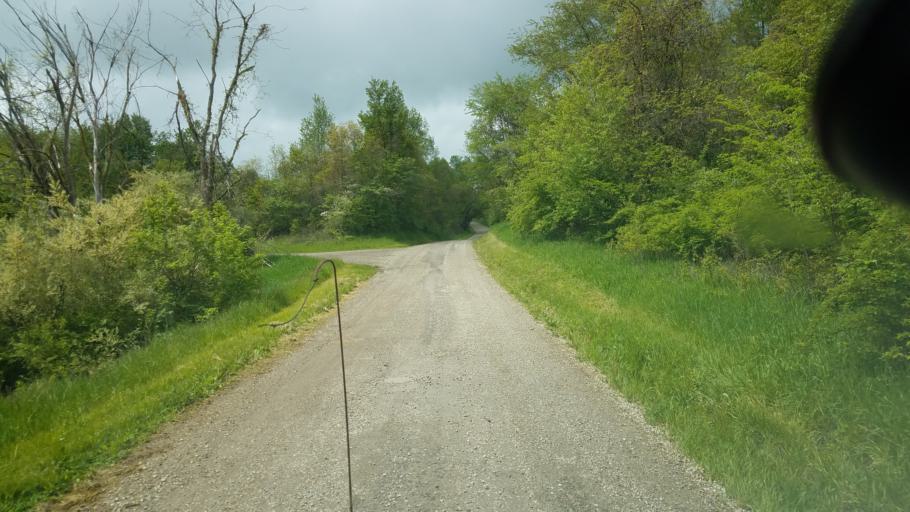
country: US
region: Ohio
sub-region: Tuscarawas County
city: Rockford
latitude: 40.4334
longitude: -81.2372
